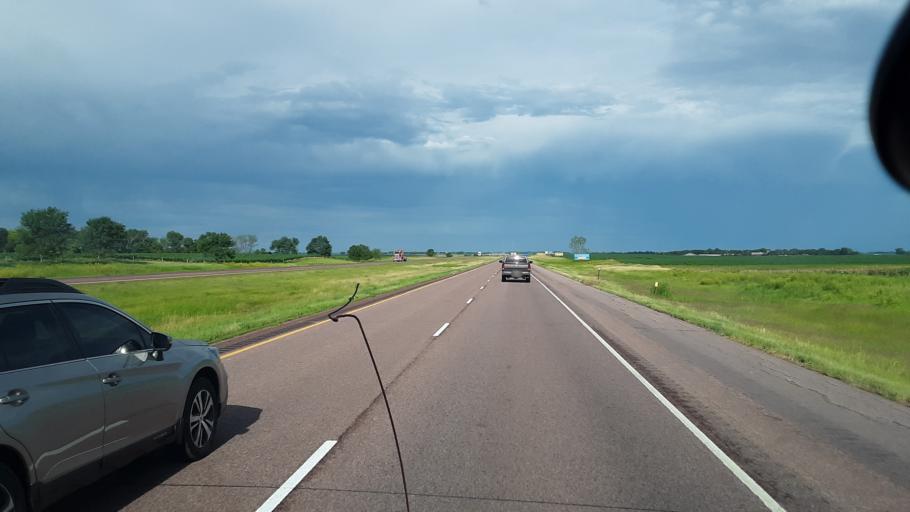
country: US
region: South Dakota
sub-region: McCook County
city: Salem
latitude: 43.6660
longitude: -97.2827
